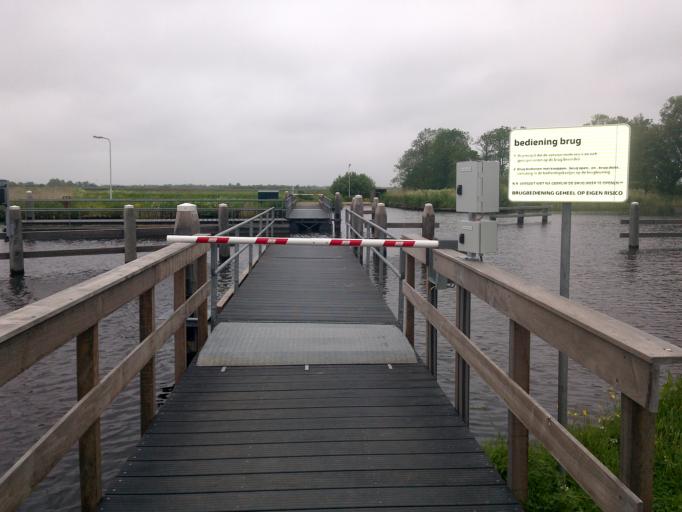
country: NL
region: Friesland
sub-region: Gemeente Boarnsterhim
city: Aldeboarn
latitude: 53.0914
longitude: 5.9066
